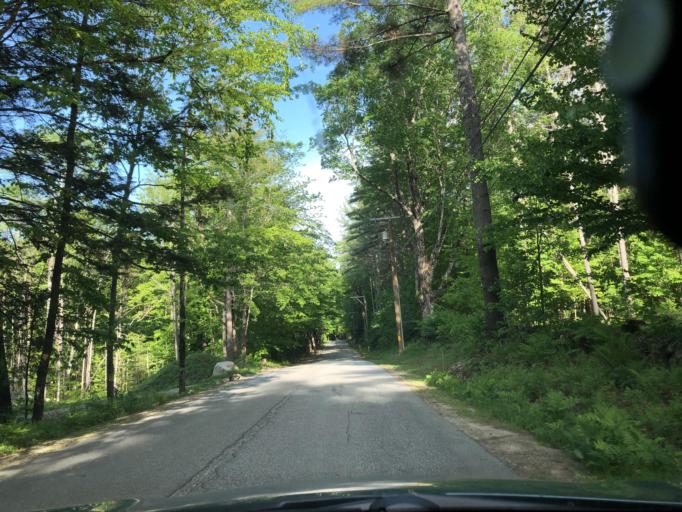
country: US
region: New Hampshire
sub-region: Merrimack County
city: New London
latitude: 43.4244
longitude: -71.9682
